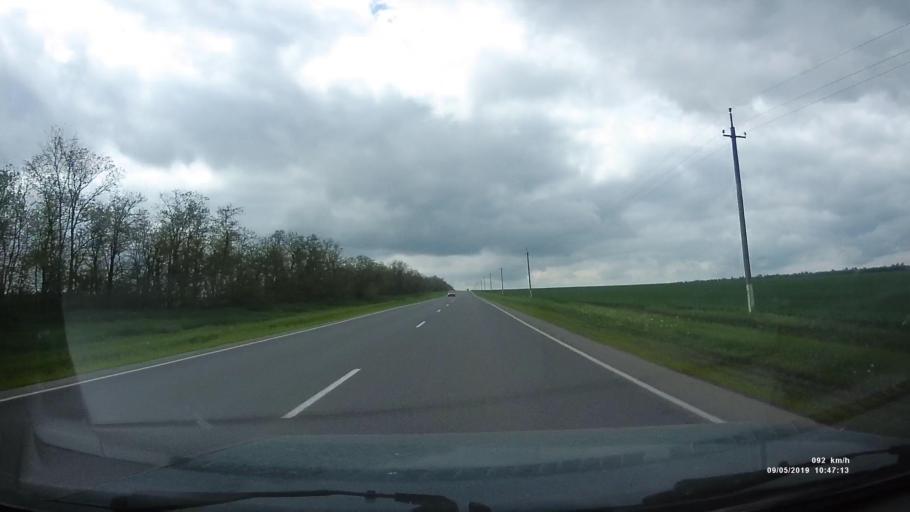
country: RU
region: Rostov
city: Peshkovo
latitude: 46.9739
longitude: 39.3556
